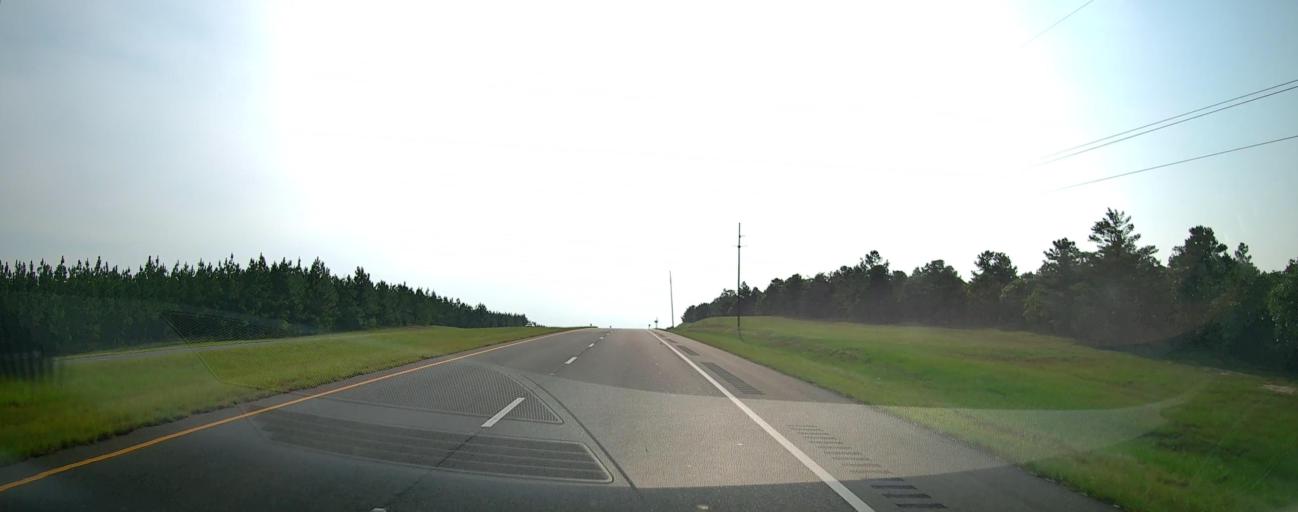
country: US
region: Georgia
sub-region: Talbot County
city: Talbotton
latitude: 32.5947
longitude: -84.4202
